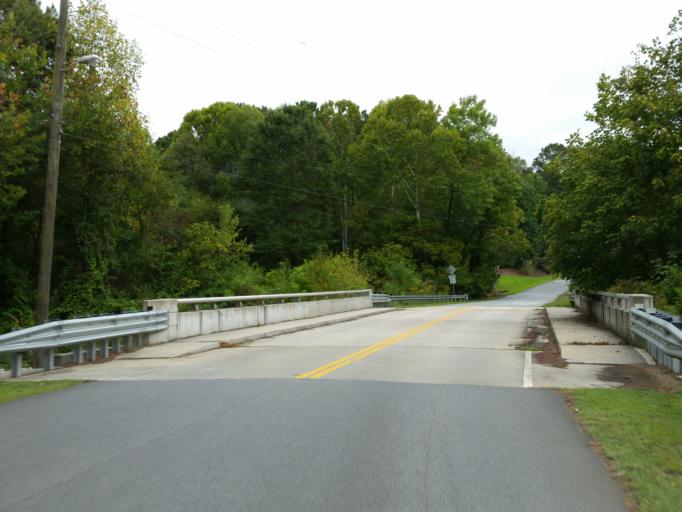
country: US
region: Georgia
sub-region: Cherokee County
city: Woodstock
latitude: 34.0317
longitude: -84.5189
